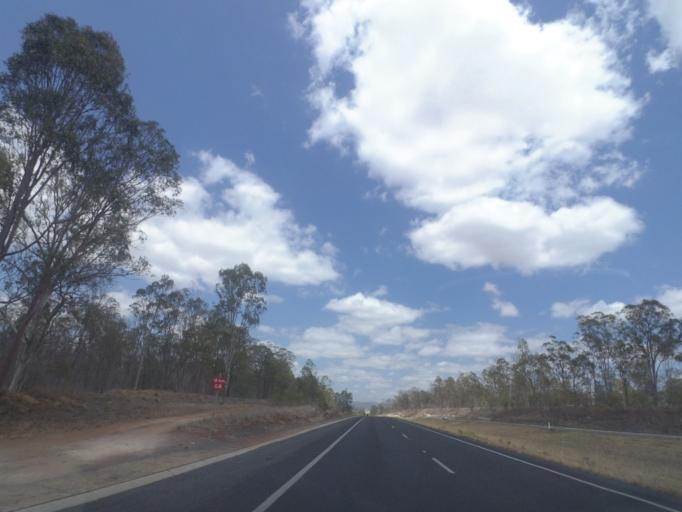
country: AU
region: Queensland
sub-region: Lockyer Valley
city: Gatton
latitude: -27.5514
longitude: 152.1400
